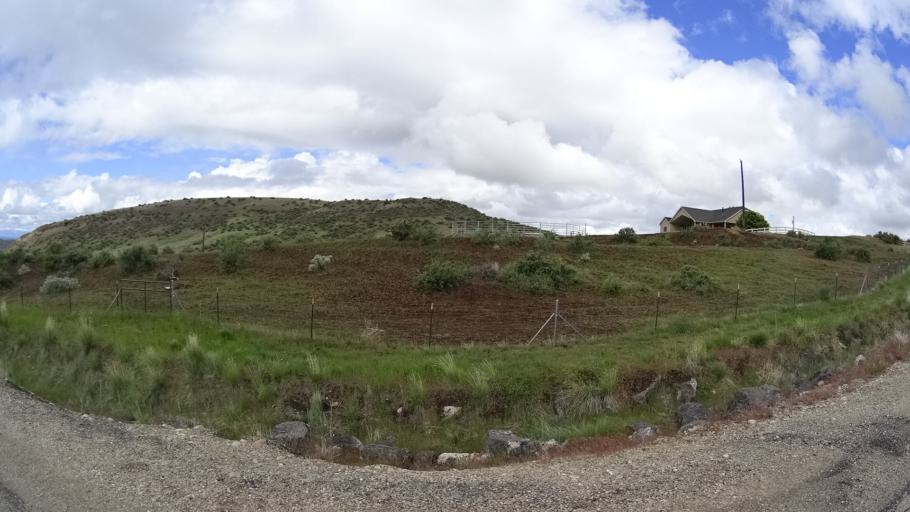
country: US
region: Idaho
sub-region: Ada County
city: Garden City
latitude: 43.7375
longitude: -116.2264
